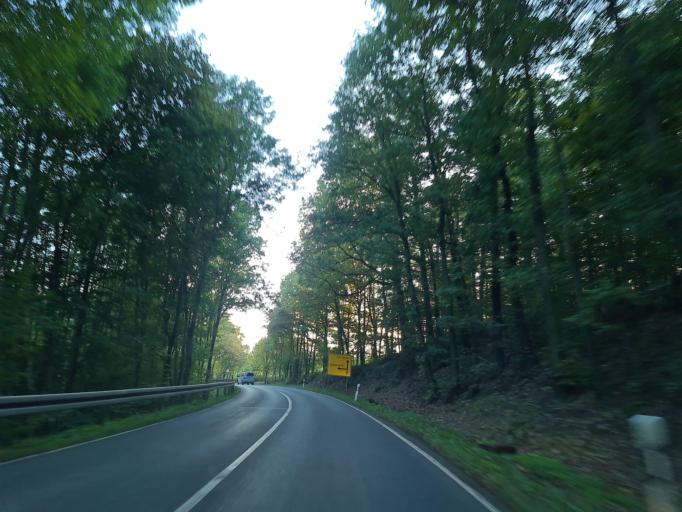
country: DE
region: Saxony
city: Elsterberg
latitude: 50.5762
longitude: 12.1287
